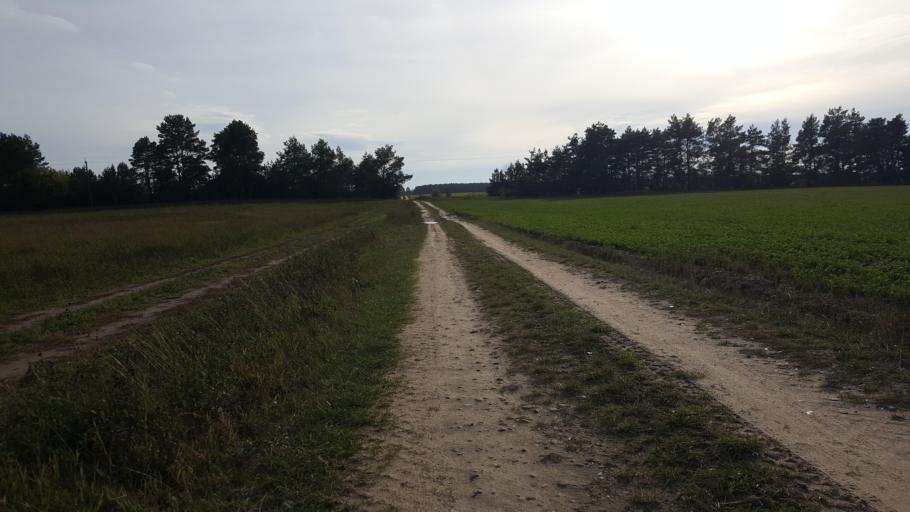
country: BY
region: Brest
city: Kamyanyets
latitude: 52.3991
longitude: 23.8559
